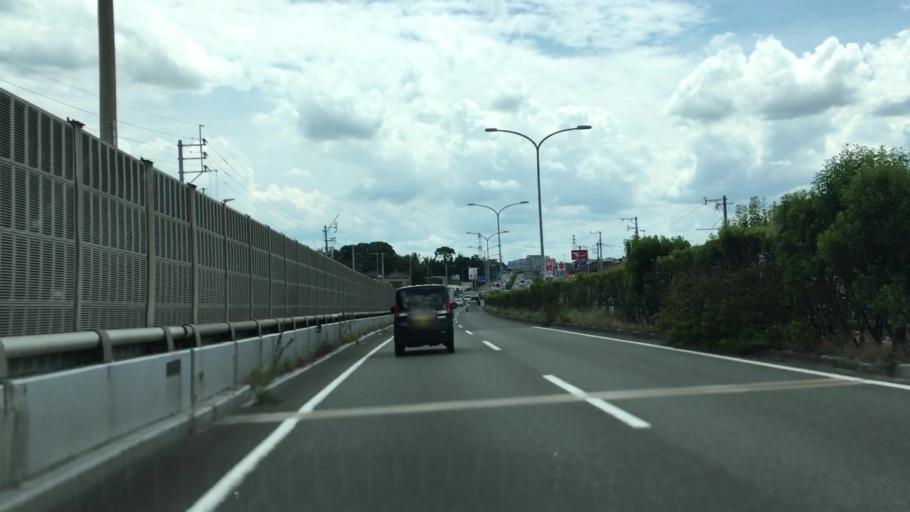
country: JP
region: Fukuoka
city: Chikushino-shi
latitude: 33.4820
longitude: 130.5384
